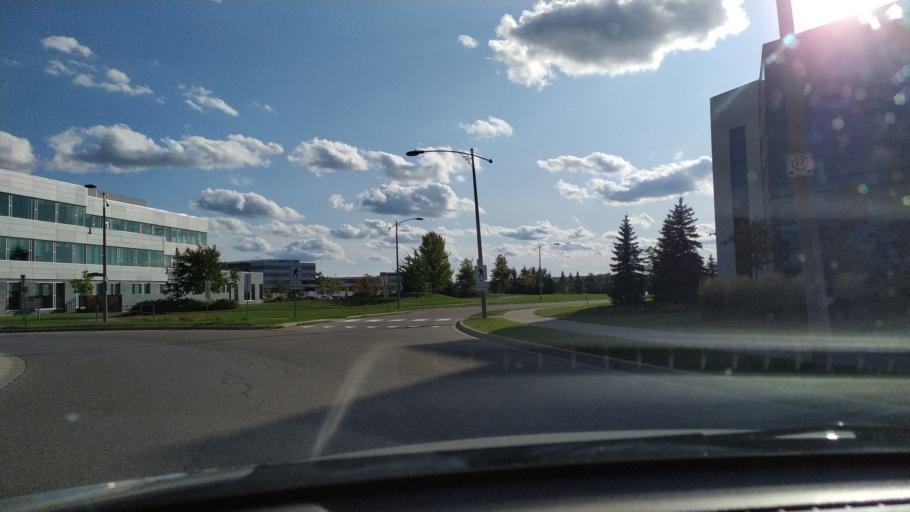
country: CA
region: Ontario
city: Waterloo
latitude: 43.4801
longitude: -80.5503
